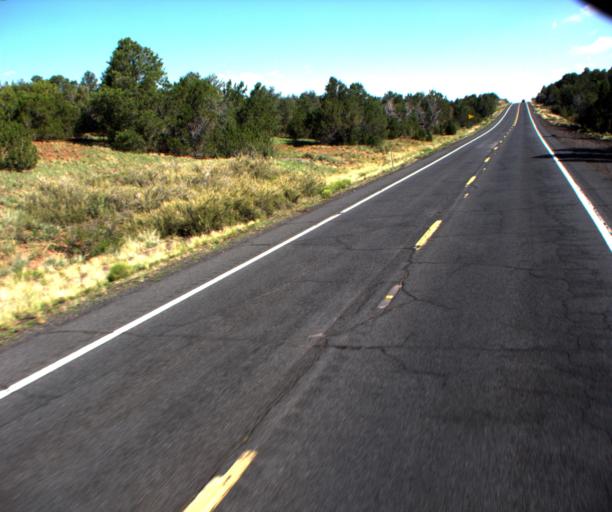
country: US
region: Arizona
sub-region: Coconino County
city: Williams
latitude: 35.4259
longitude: -112.1707
